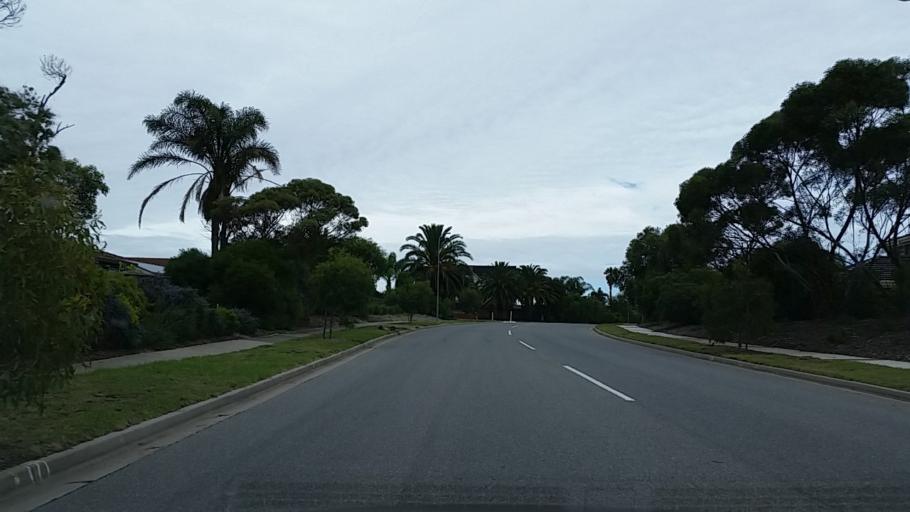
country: AU
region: South Australia
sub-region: Charles Sturt
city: West Lakes Shore
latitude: -34.8607
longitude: 138.4965
